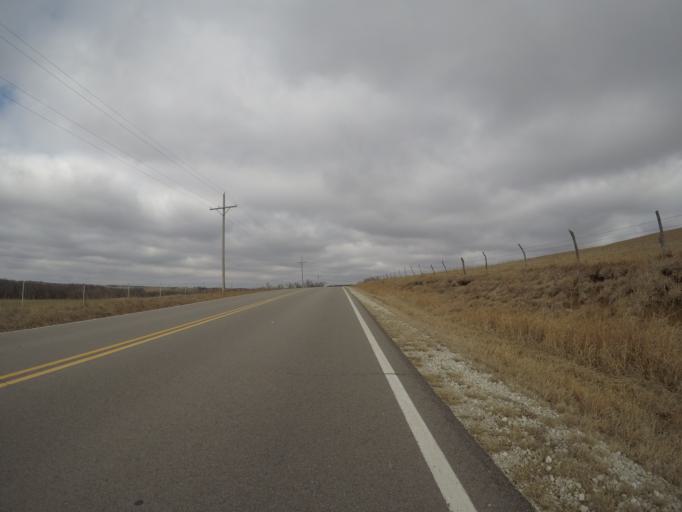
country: US
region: Kansas
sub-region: Pottawatomie County
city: Westmoreland
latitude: 39.4102
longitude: -96.4521
